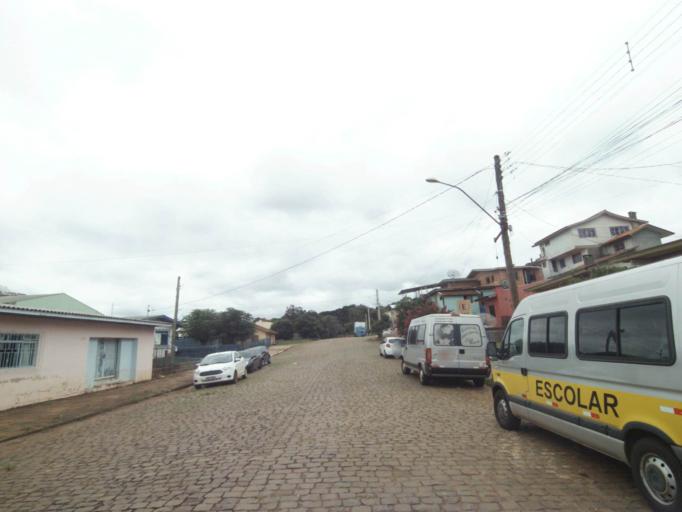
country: BR
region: Rio Grande do Sul
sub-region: Lagoa Vermelha
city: Lagoa Vermelha
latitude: -28.2066
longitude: -51.5253
